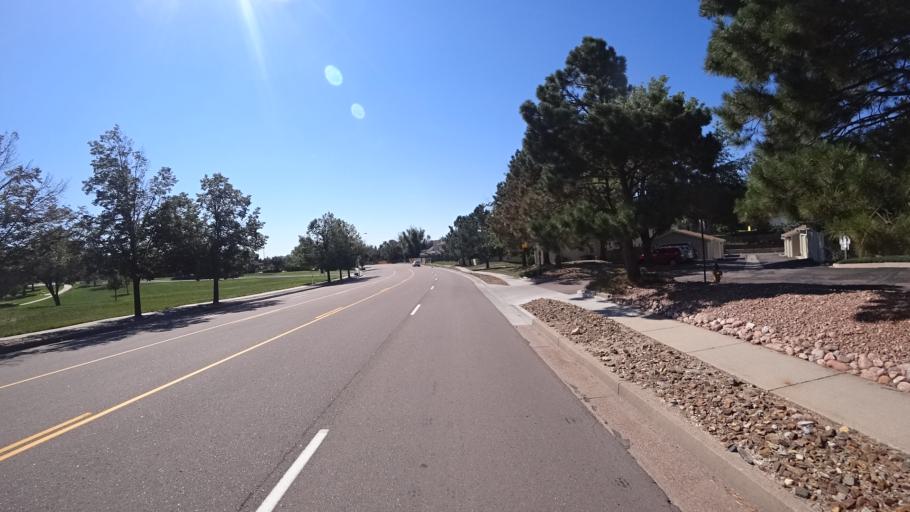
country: US
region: Colorado
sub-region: El Paso County
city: Black Forest
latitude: 38.9473
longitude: -104.7687
